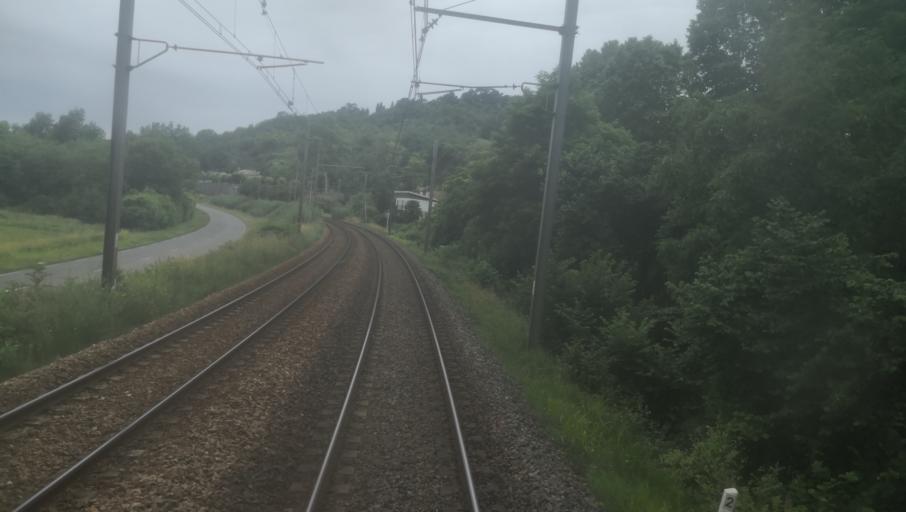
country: FR
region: Aquitaine
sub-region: Departement du Lot-et-Garonne
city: Port-Sainte-Marie
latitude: 44.2504
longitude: 0.4088
